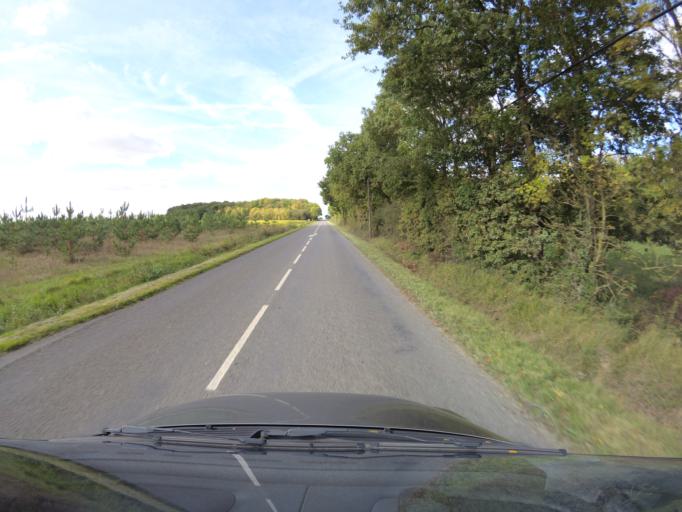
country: FR
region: Pays de la Loire
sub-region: Departement de la Loire-Atlantique
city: Gorges
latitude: 47.1042
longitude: -1.3223
